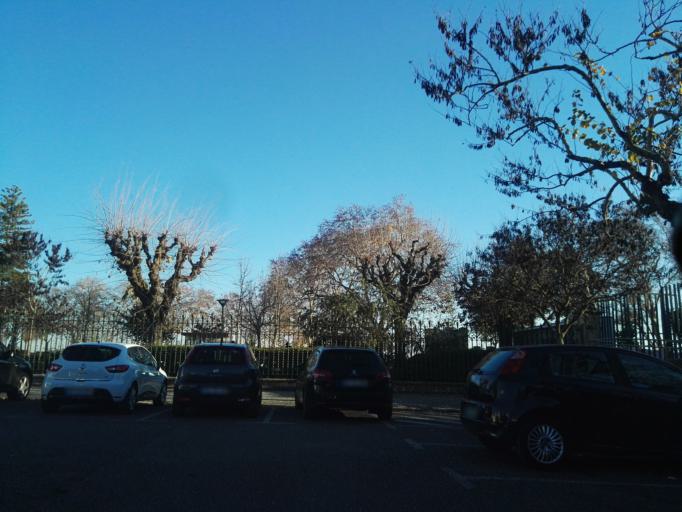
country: PT
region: Santarem
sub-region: Santarem
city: Santarem
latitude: 39.2341
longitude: -8.6768
